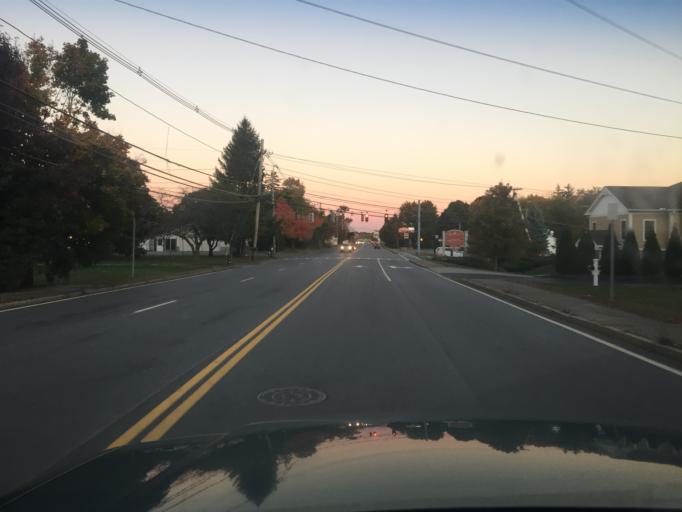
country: US
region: Massachusetts
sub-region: Worcester County
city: Milford
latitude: 42.1490
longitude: -71.4977
